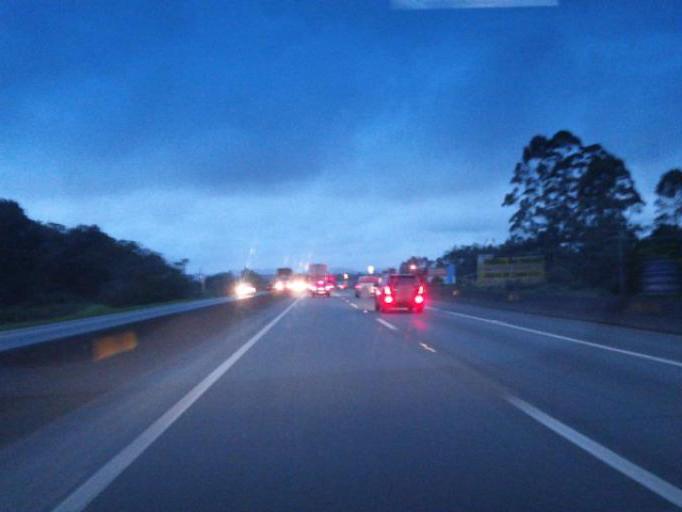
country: BR
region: Santa Catarina
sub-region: Penha
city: Penha
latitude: -26.7410
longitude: -48.6983
